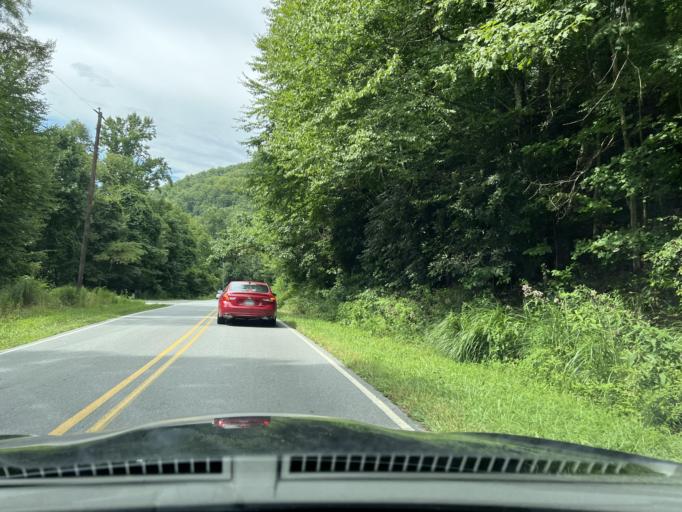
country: US
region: North Carolina
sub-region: Henderson County
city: Fruitland
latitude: 35.4235
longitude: -82.4190
